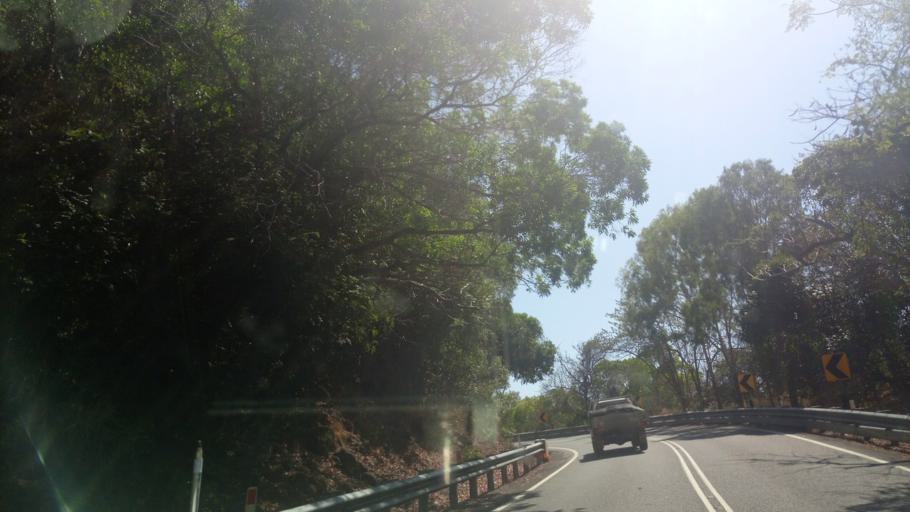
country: AU
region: Queensland
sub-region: Cairns
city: Palm Cove
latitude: -16.6527
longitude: 145.5639
